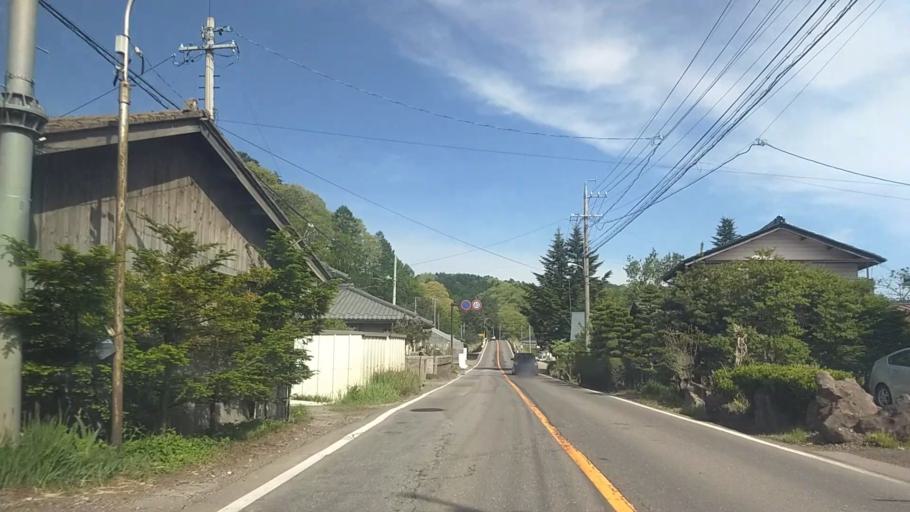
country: JP
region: Nagano
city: Saku
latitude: 36.0368
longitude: 138.4750
